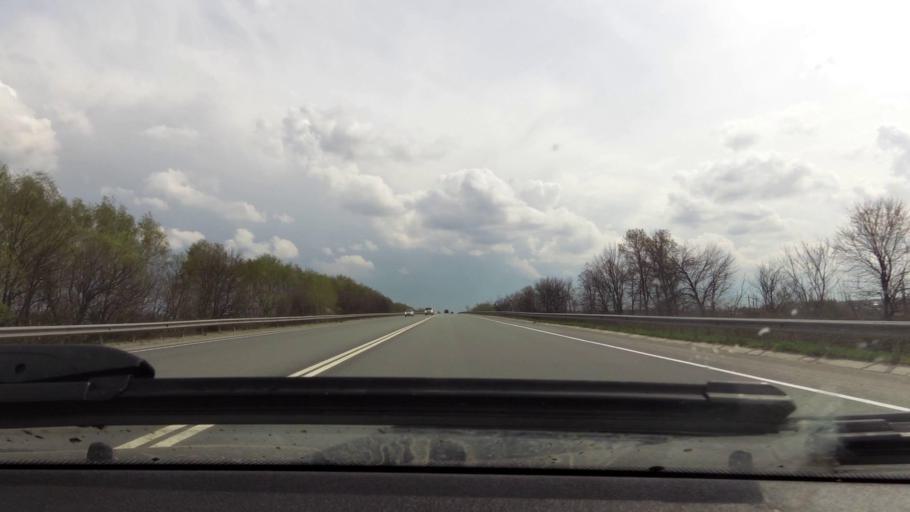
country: RU
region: Rjazan
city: Bagramovo
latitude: 54.7389
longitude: 39.4471
